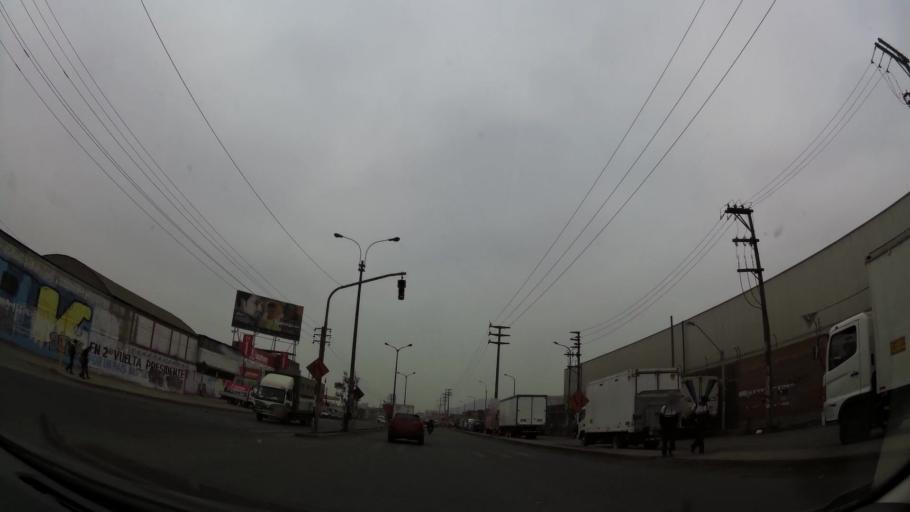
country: PE
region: Lima
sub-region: Lima
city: Vitarte
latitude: -12.0502
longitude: -76.9536
